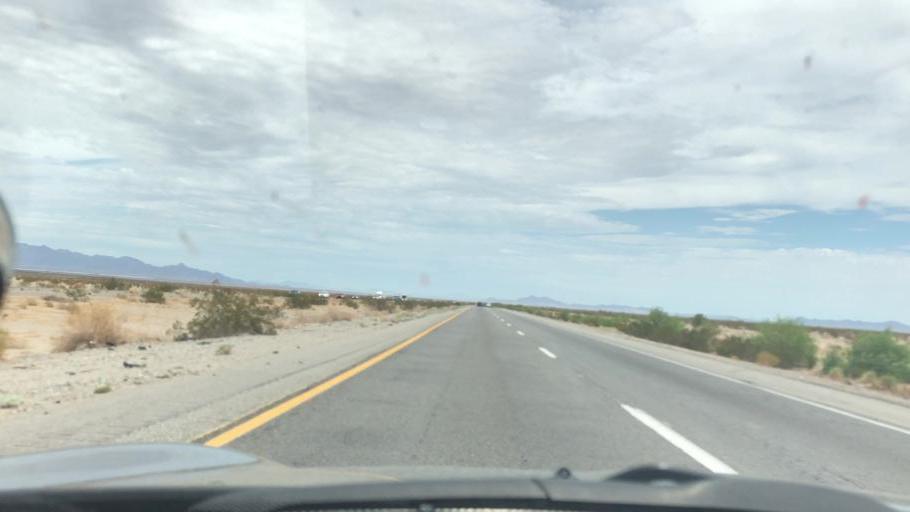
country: US
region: California
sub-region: Riverside County
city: Mesa Verde
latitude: 33.6490
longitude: -115.1310
